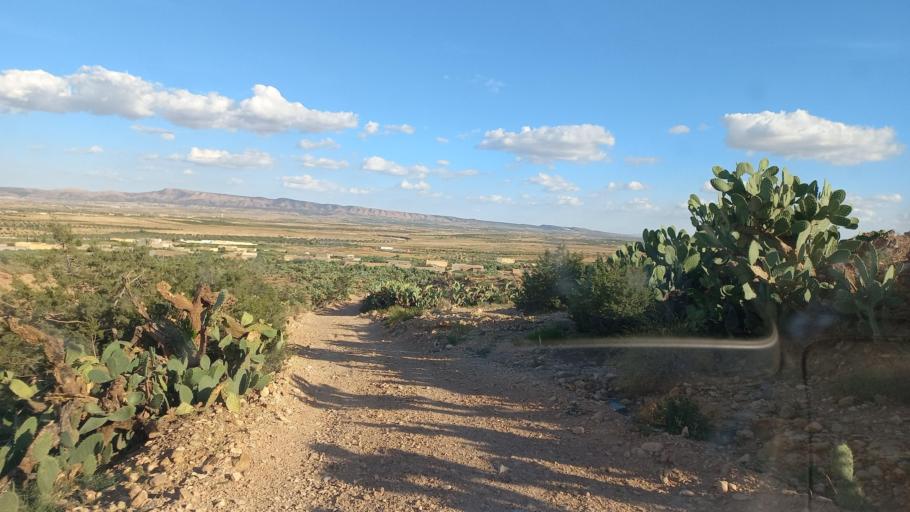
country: TN
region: Al Qasrayn
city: Sbiba
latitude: 35.3828
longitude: 9.0189
